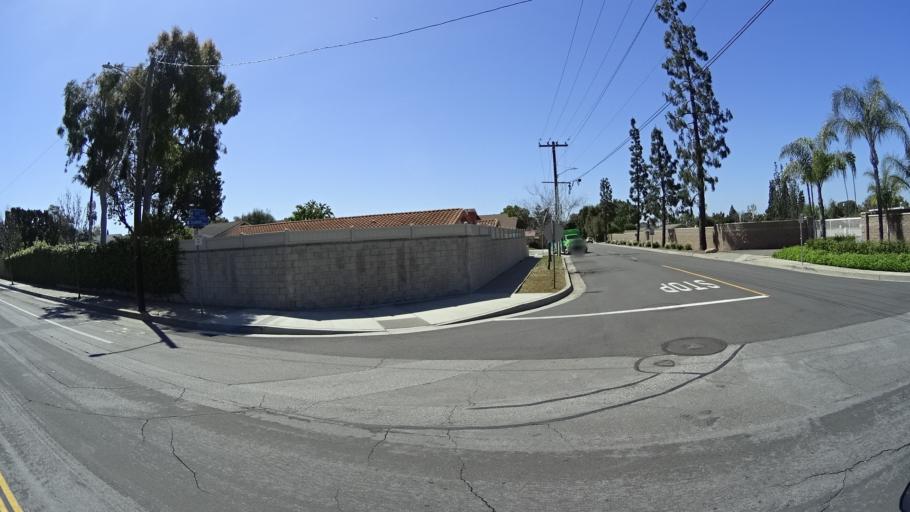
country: US
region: California
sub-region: Orange County
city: Villa Park
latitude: 33.8181
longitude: -117.8008
